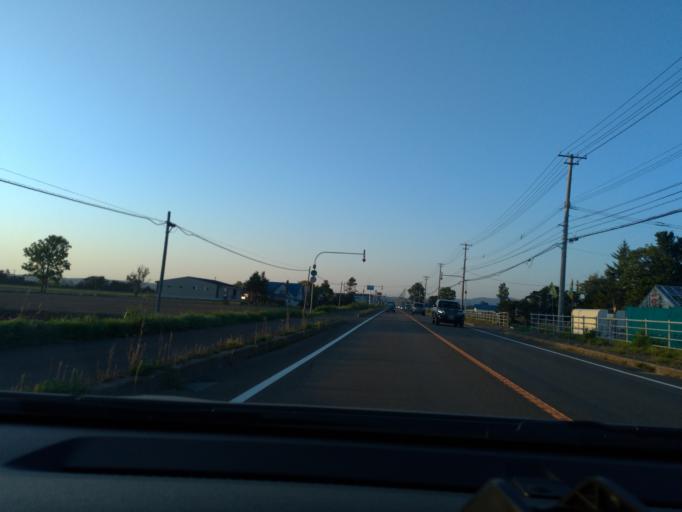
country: JP
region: Hokkaido
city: Tobetsu
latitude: 43.1970
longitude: 141.5229
